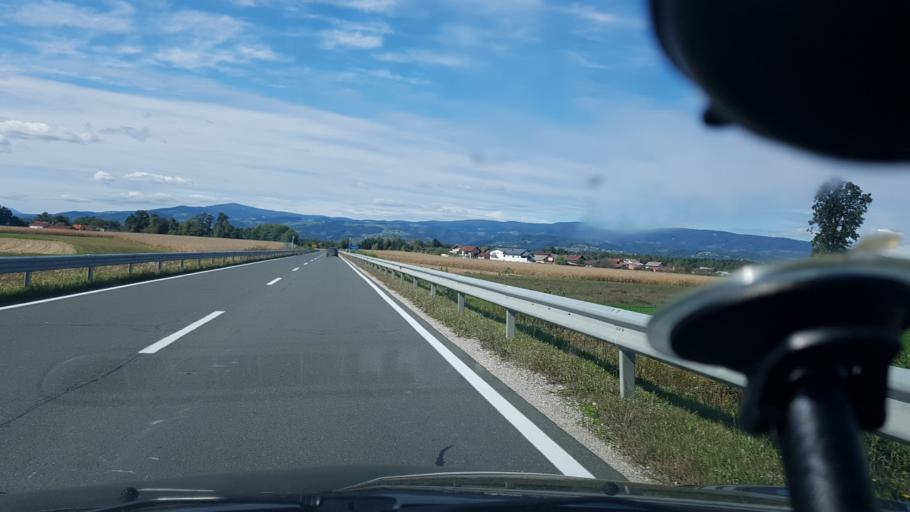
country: SI
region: Slovenska Bistrica
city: Pragersko
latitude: 46.4101
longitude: 15.6946
